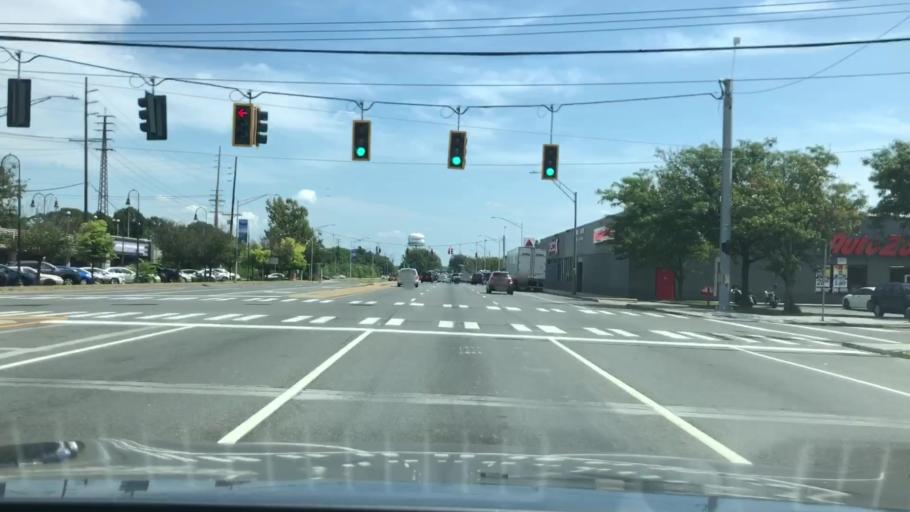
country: US
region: New York
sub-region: Nassau County
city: Baldwin
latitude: 40.6562
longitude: -73.6071
